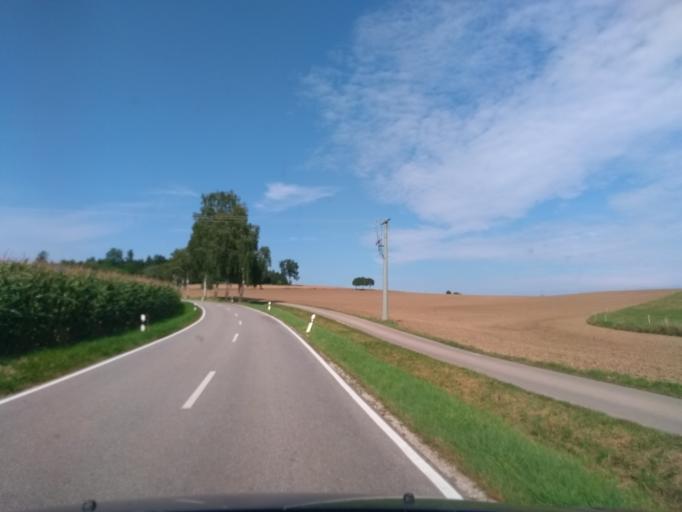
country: DE
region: Bavaria
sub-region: Upper Bavaria
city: Schwabhausen
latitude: 48.3964
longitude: 11.3484
